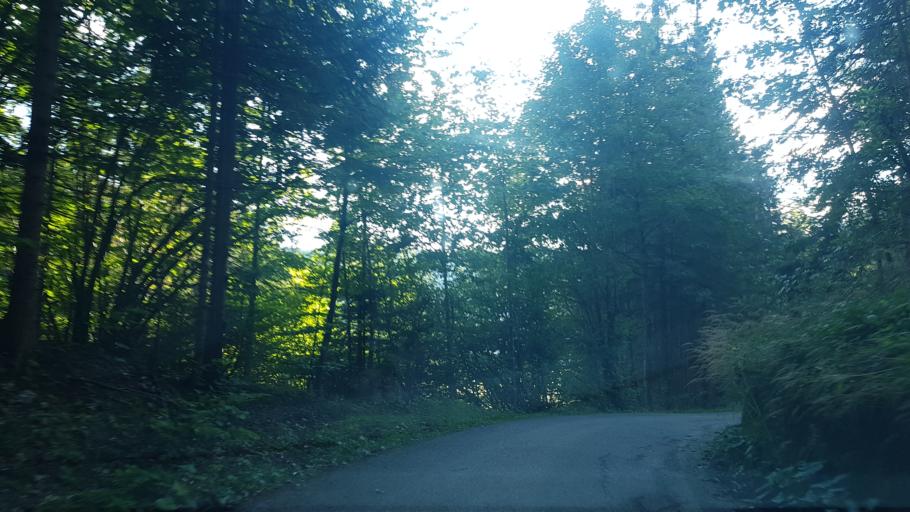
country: IT
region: Friuli Venezia Giulia
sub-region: Provincia di Udine
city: Tarvisio
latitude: 46.4922
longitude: 13.5968
